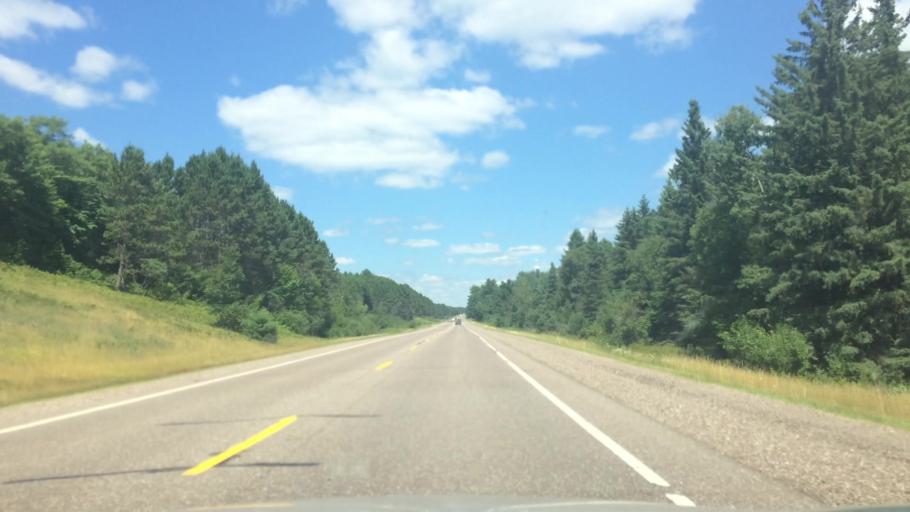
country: US
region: Wisconsin
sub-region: Vilas County
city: Lac du Flambeau
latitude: 45.9556
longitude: -89.7006
